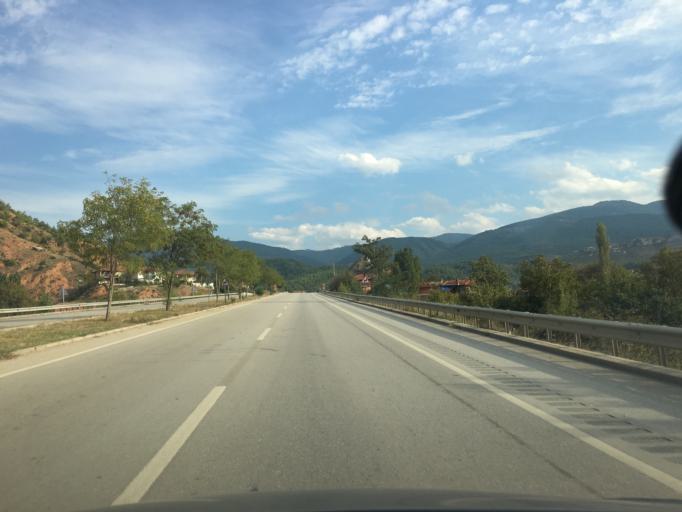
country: TR
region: Karabuk
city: Karabuk
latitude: 41.0982
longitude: 32.6736
